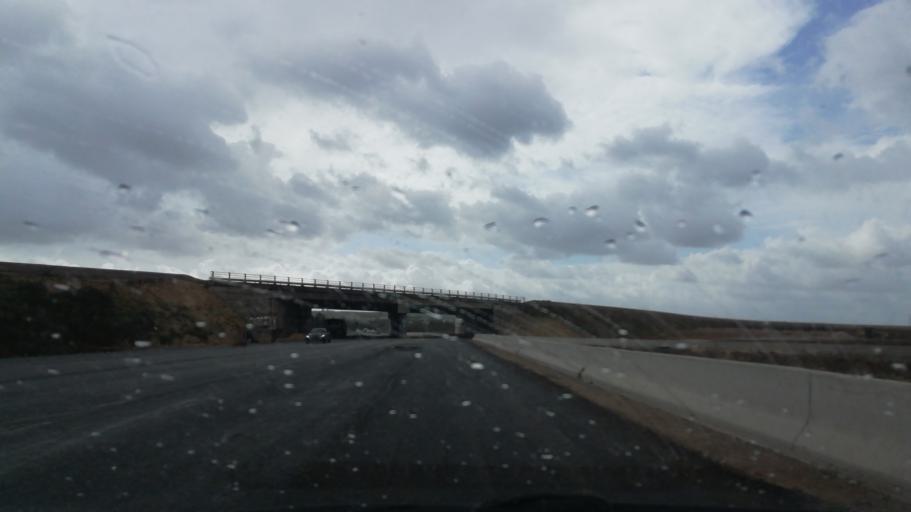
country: DZ
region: Oran
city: Sidi ech Chahmi
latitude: 35.6436
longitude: -0.5257
